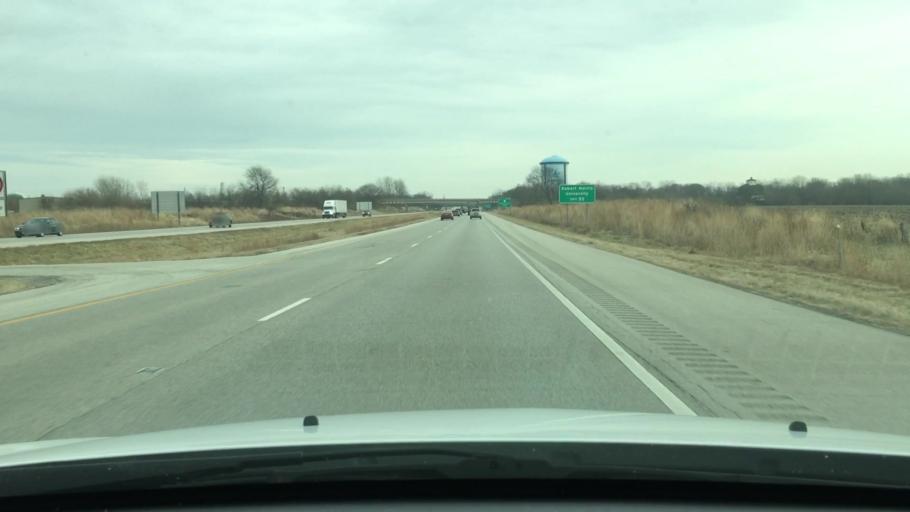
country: US
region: Illinois
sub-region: Sangamon County
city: Jerome
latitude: 39.7486
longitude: -89.7257
